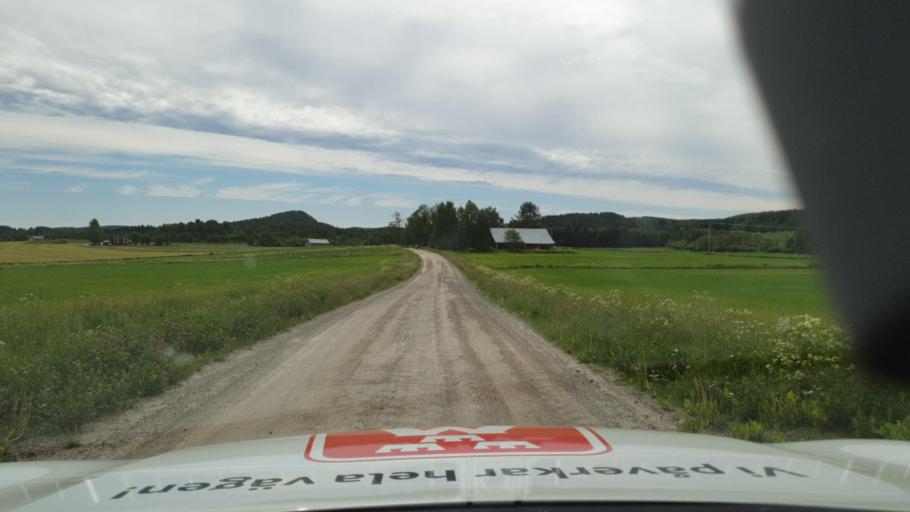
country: SE
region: Vaesterbotten
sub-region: Robertsfors Kommun
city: Robertsfors
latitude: 64.2689
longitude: 20.6322
